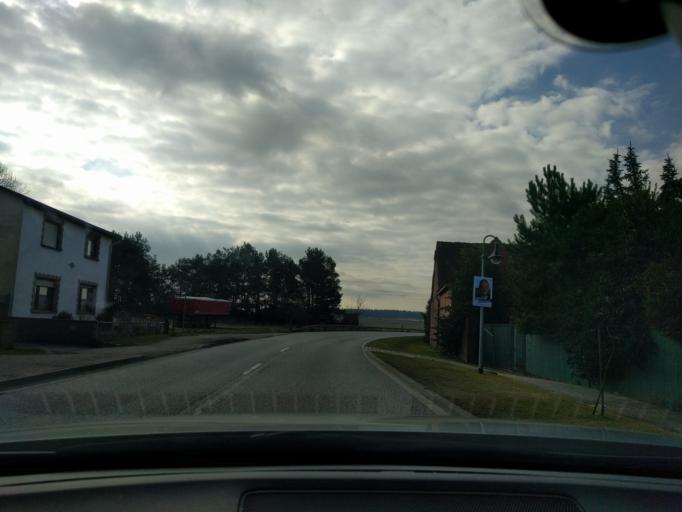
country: DE
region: Saxony-Anhalt
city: Burgstall
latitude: 52.4095
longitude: 11.6248
